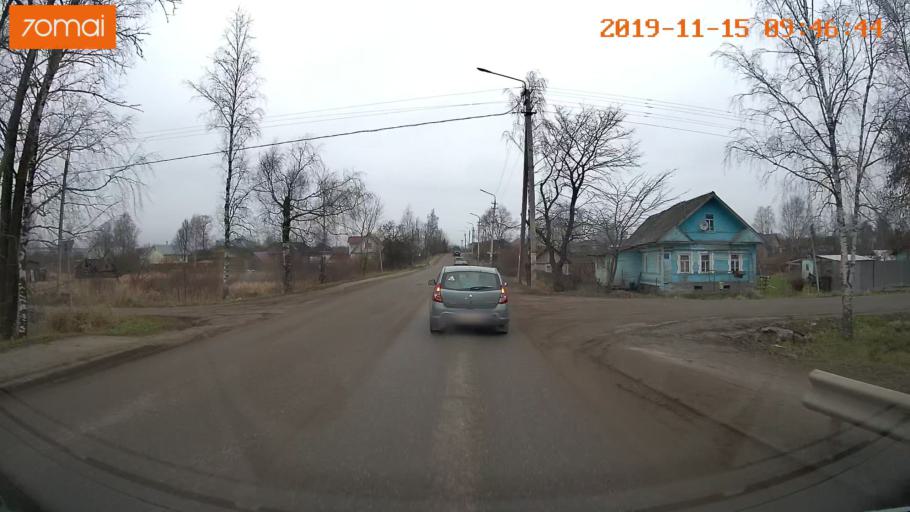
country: RU
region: Vologda
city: Sheksna
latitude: 59.2122
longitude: 38.5109
